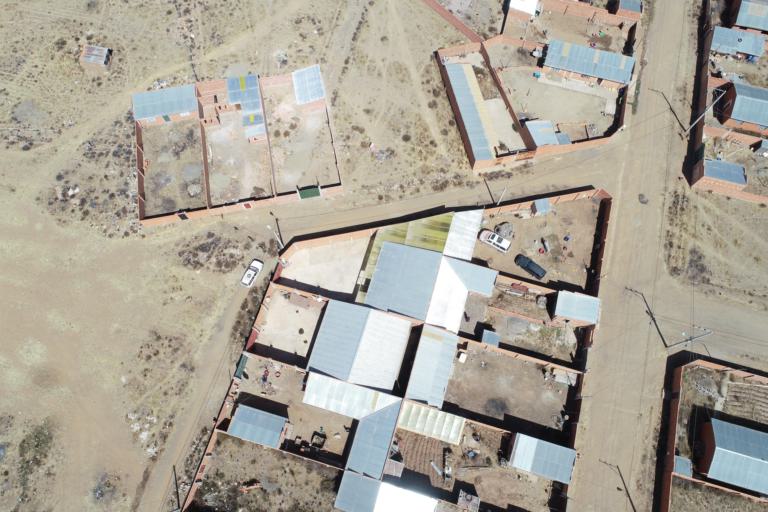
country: BO
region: La Paz
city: La Paz
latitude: -16.5944
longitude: -68.2107
